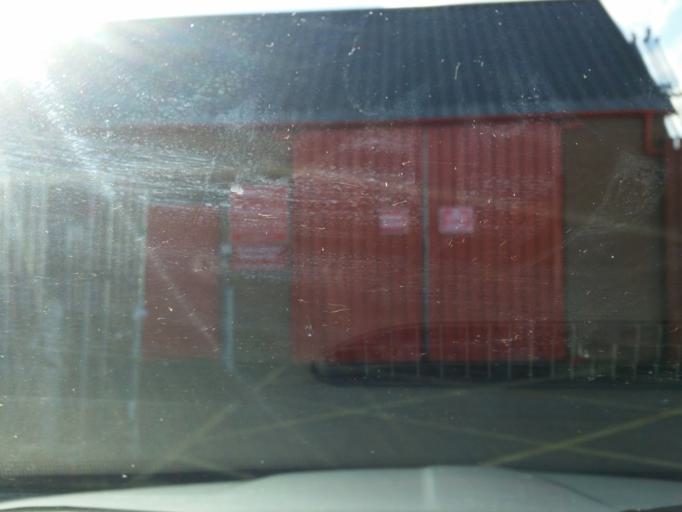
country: GB
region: Northern Ireland
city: Lisnaskea
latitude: 54.2553
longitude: -7.4478
